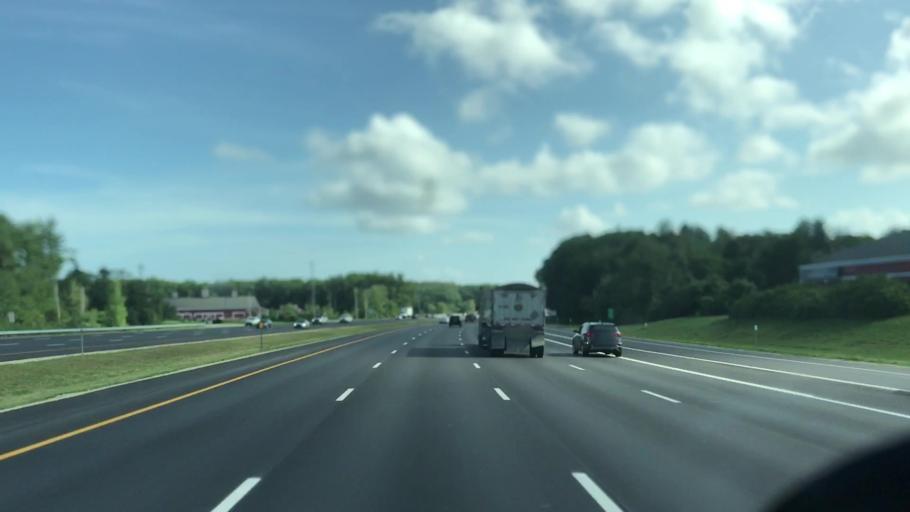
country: US
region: New Hampshire
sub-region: Rockingham County
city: Hampton Falls
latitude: 42.9380
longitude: -70.8616
